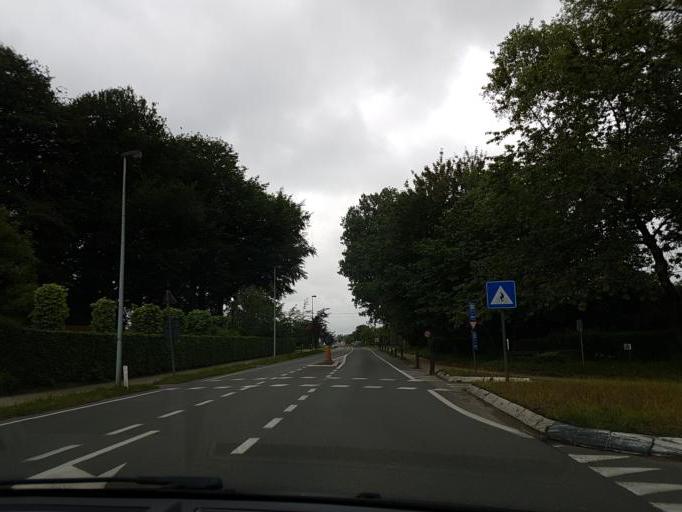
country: BE
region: Flanders
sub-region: Provincie West-Vlaanderen
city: Beernem
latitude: 51.1255
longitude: 3.3515
